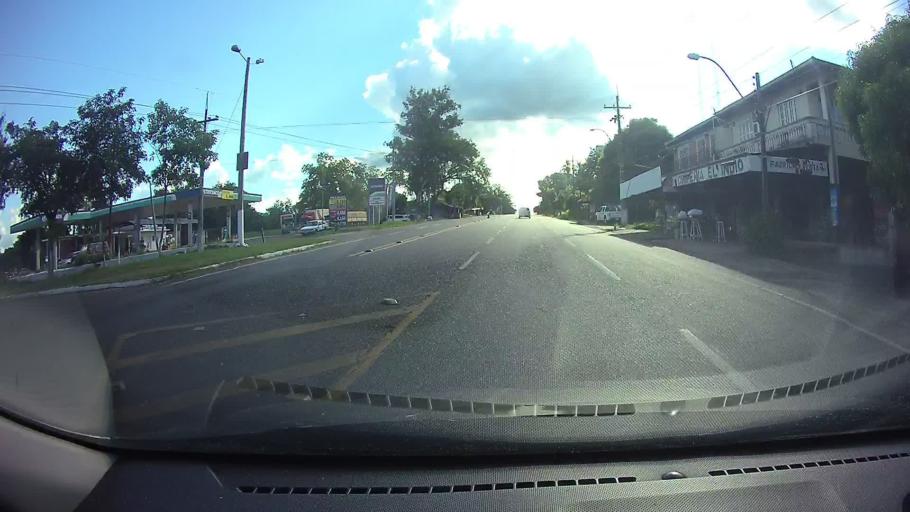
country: PY
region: Cordillera
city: Eusebio Ayala
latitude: -25.3820
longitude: -57.0448
